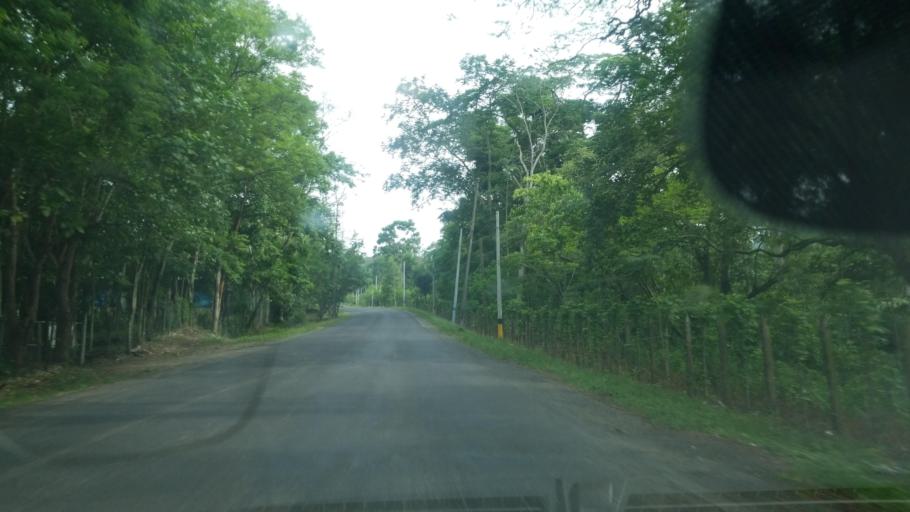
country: HN
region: Santa Barbara
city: Petoa
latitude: 15.2317
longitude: -88.2672
